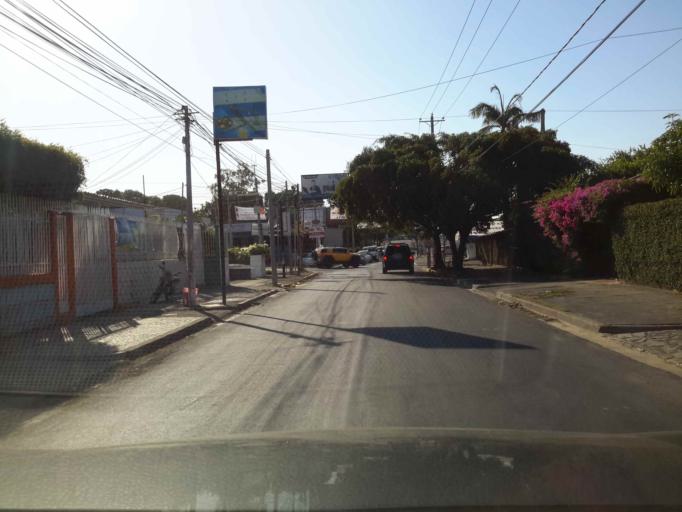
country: NI
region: Managua
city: Managua
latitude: 12.1196
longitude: -86.2544
